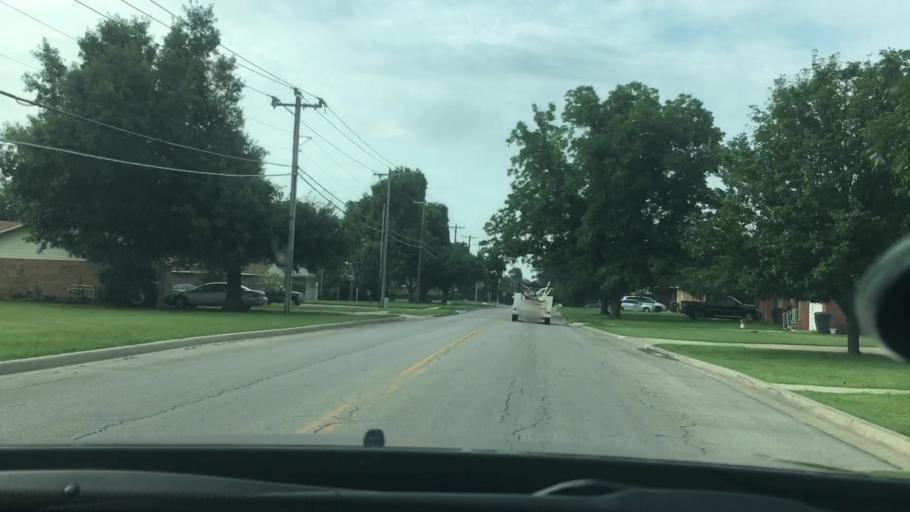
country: US
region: Oklahoma
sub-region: Carter County
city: Ardmore
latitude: 34.1946
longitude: -97.1255
